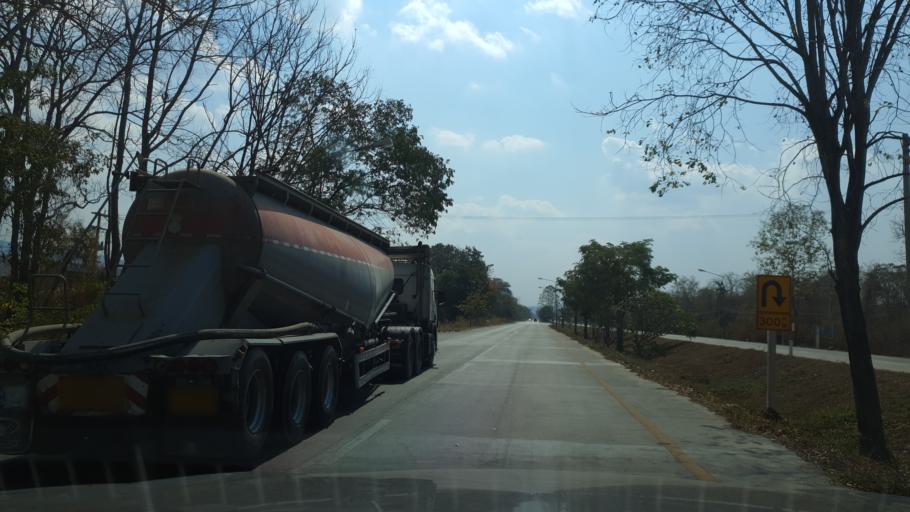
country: TH
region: Lampang
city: Mae Phrik
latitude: 17.4432
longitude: 99.1592
